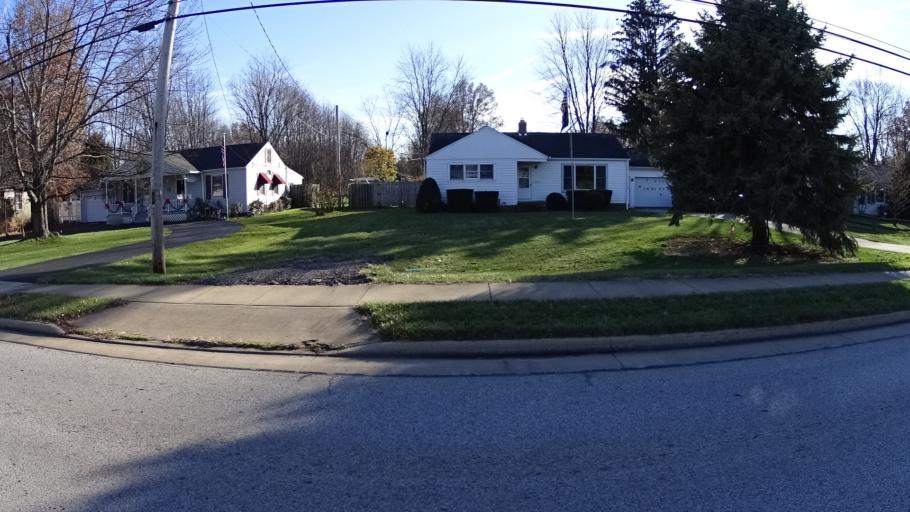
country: US
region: Ohio
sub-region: Lorain County
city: North Ridgeville
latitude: 41.3851
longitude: -81.9897
